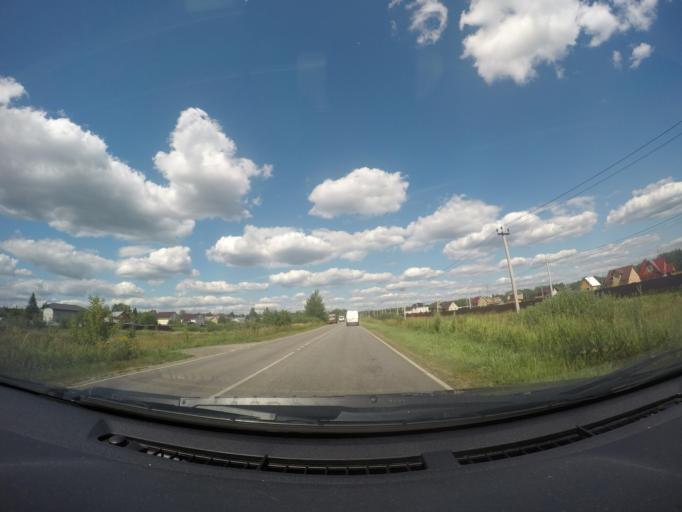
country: RU
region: Moskovskaya
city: Rechitsy
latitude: 55.5974
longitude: 38.5230
